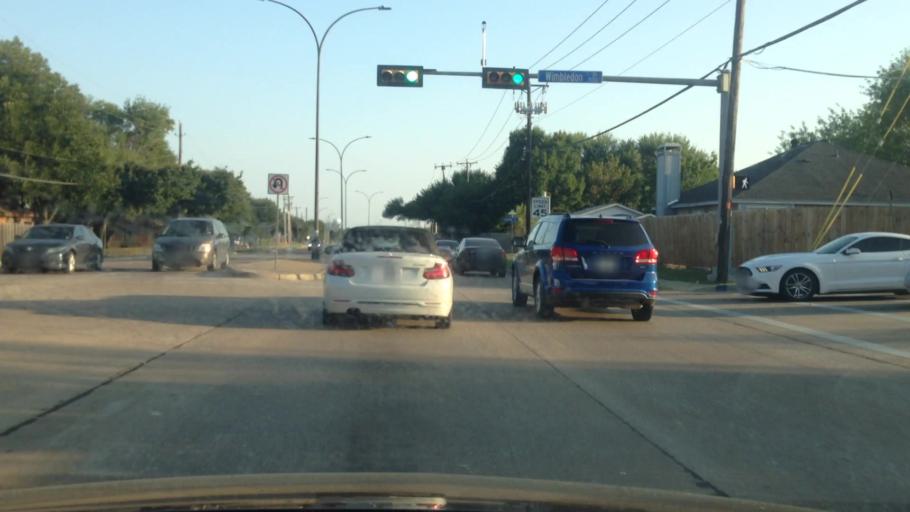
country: US
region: Texas
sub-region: Tarrant County
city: Dalworthington Gardens
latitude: 32.6630
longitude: -97.1151
